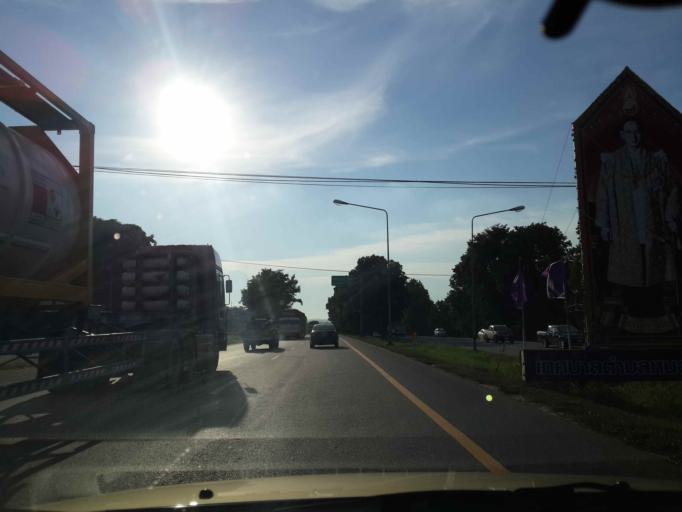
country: TH
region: Chon Buri
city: Bang Lamung
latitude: 12.9850
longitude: 100.9500
